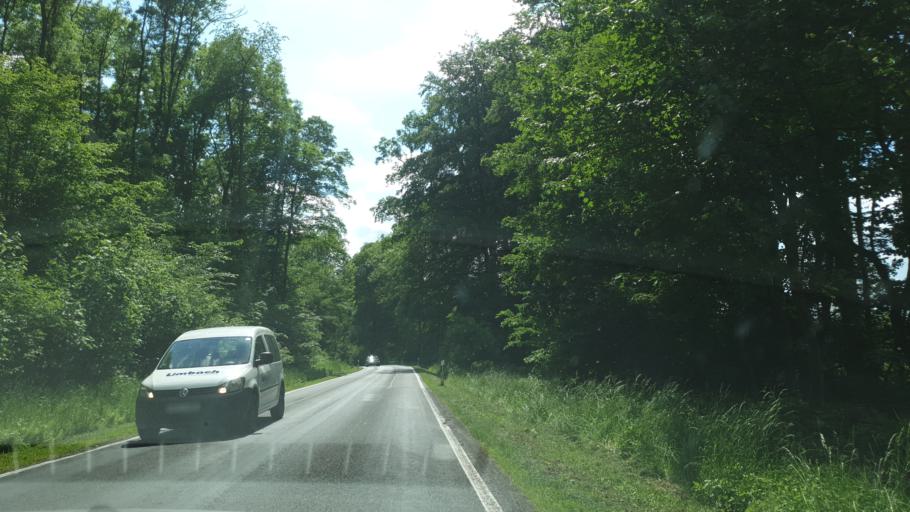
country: DE
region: Rheinland-Pfalz
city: Quirnbach
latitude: 50.5042
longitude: 7.8059
